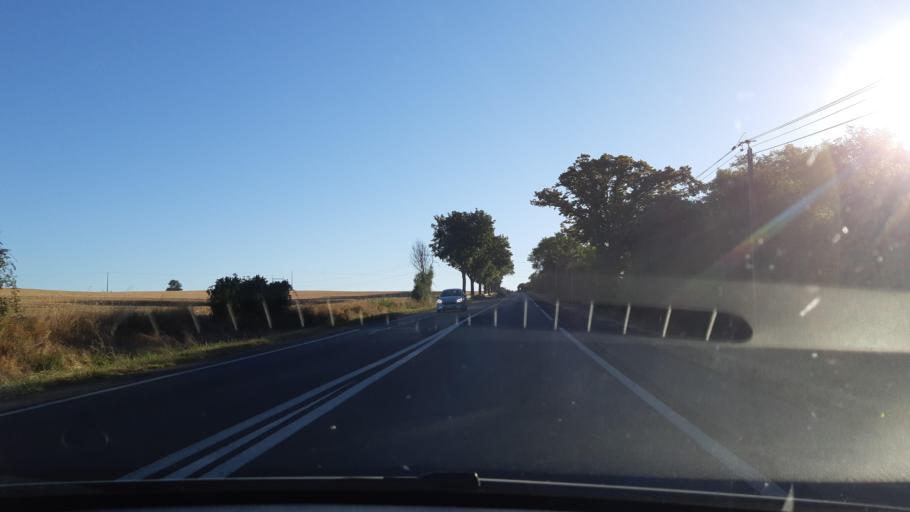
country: FR
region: Poitou-Charentes
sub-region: Departement des Deux-Sevres
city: La Creche
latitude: 46.3752
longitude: -0.2803
